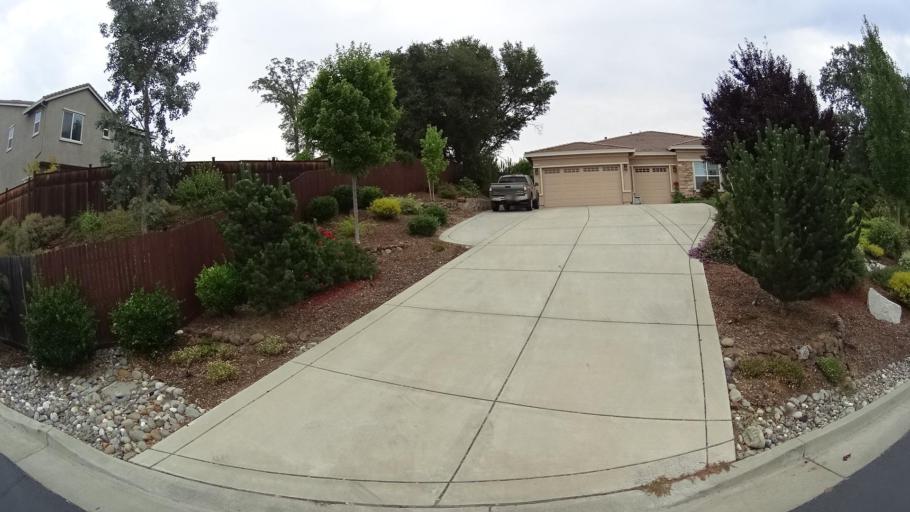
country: US
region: California
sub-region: Placer County
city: Rocklin
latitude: 38.7795
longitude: -121.2268
